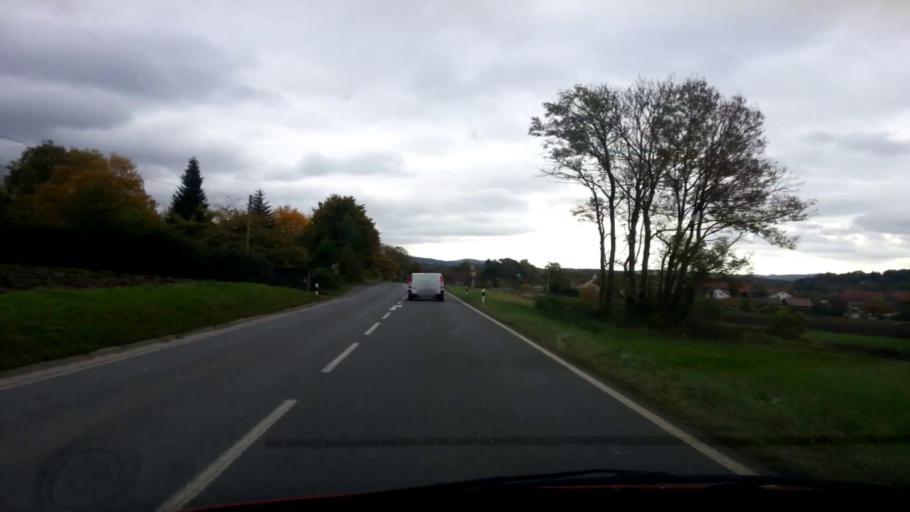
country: DE
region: Bavaria
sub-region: Upper Franconia
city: Reuth
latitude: 49.9730
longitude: 11.6821
